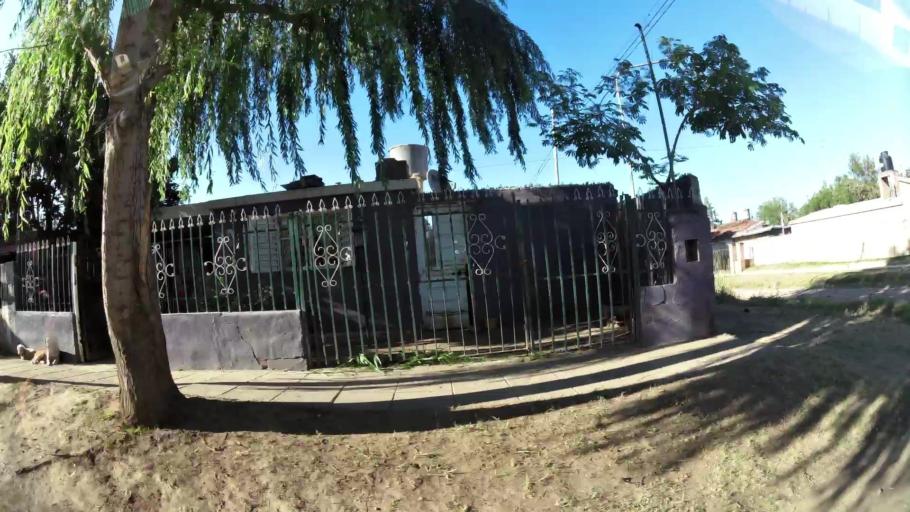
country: AR
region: Cordoba
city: Villa Allende
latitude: -31.3300
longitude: -64.2414
